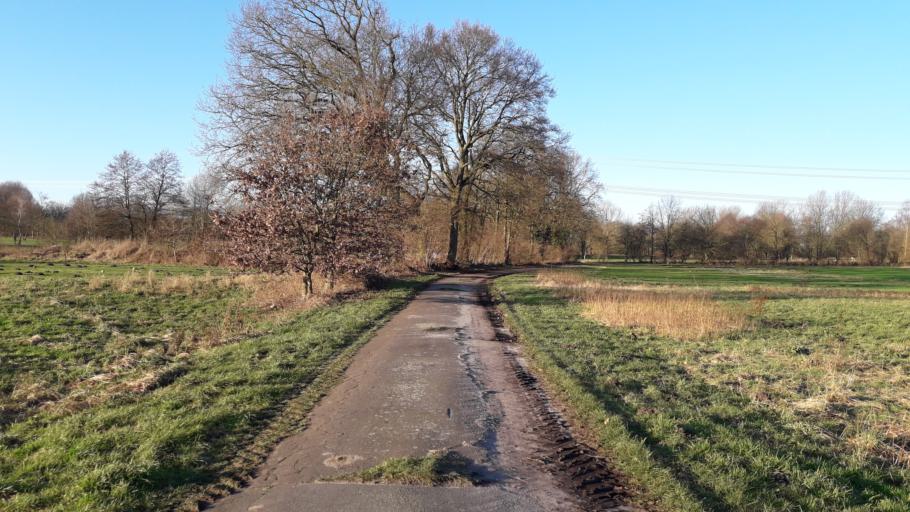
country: DE
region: Schleswig-Holstein
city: Quickborn
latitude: 53.7153
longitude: 9.8617
